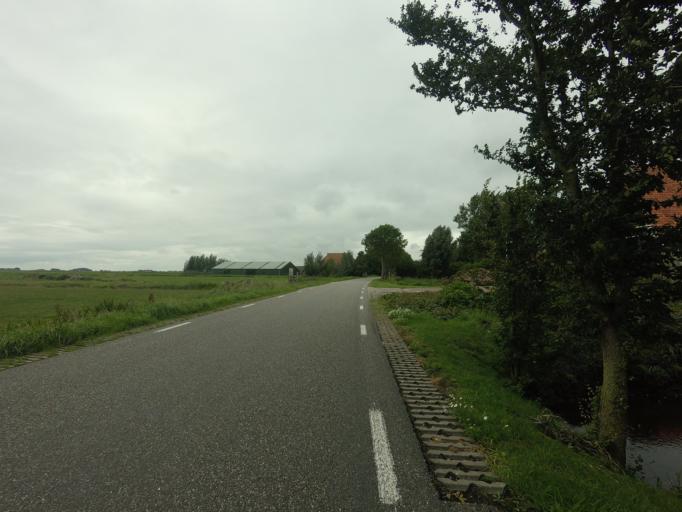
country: NL
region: Friesland
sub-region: Sudwest Fryslan
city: Heeg
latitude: 52.9673
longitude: 5.5737
